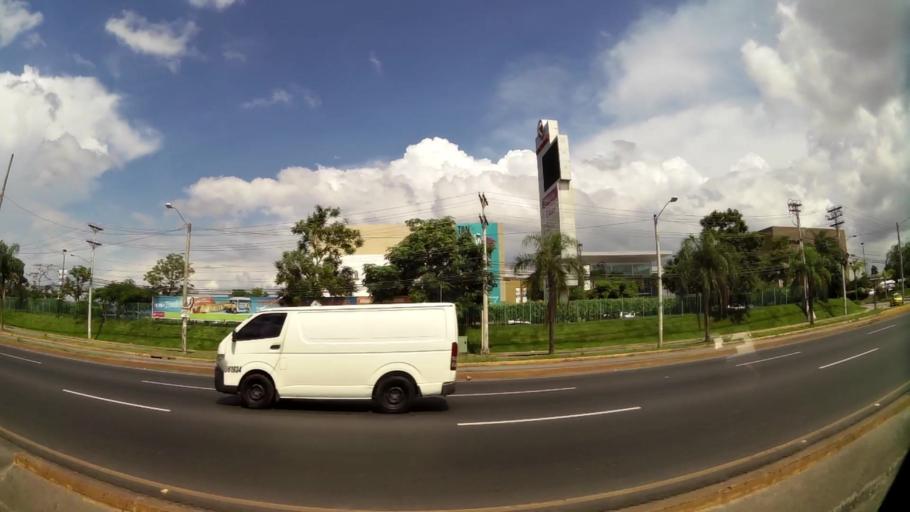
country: PA
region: Panama
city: San Miguelito
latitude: 9.0505
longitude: -79.4519
